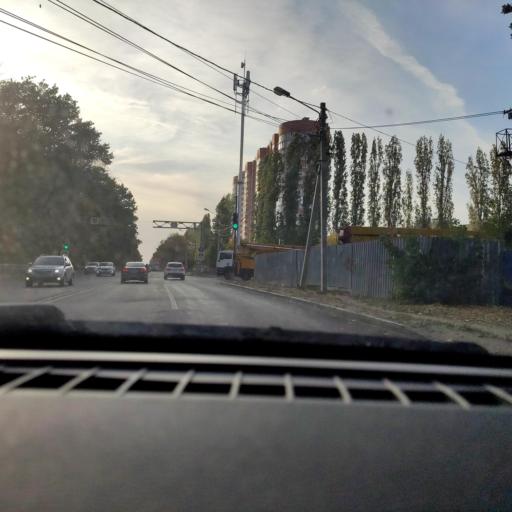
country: RU
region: Voronezj
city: Voronezh
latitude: 51.7264
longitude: 39.2133
